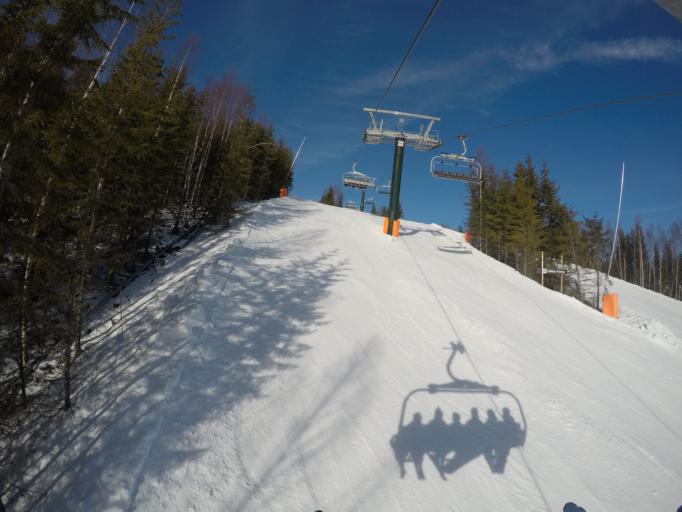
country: SE
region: Dalarna
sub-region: Borlange Kommun
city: Borlaenge
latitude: 60.3799
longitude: 15.4022
